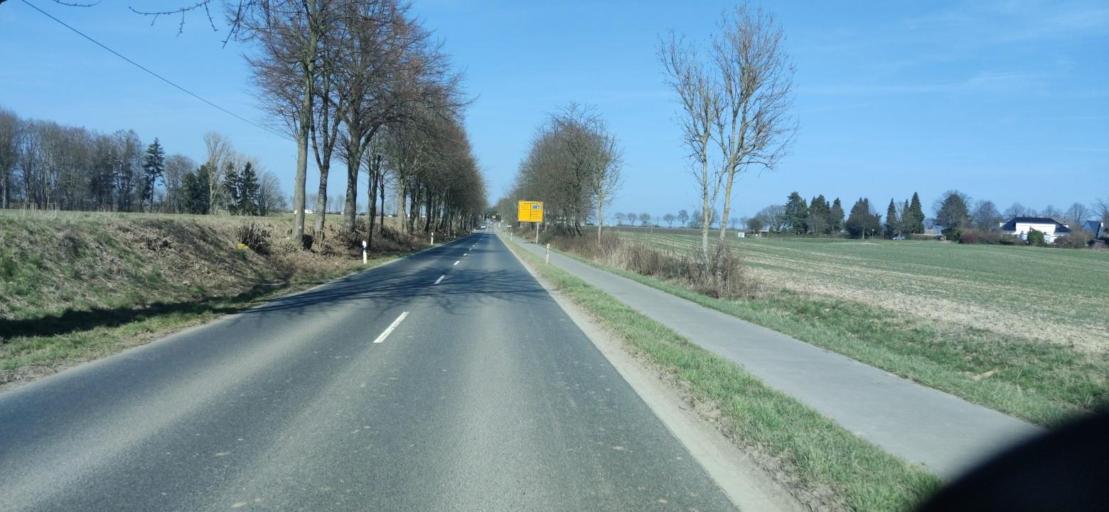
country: DE
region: North Rhine-Westphalia
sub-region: Regierungsbezirk Dusseldorf
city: Erkrath
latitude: 51.2561
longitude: 6.9031
